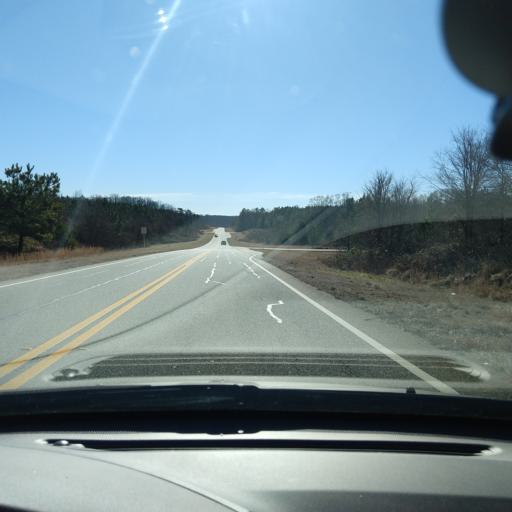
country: US
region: Georgia
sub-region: Walton County
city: Social Circle
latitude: 33.6711
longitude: -83.6963
